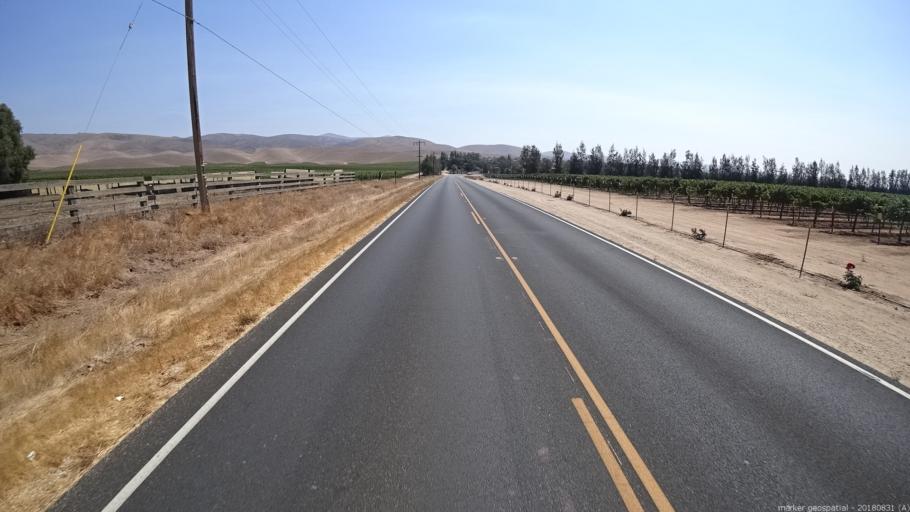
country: US
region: California
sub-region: Monterey County
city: Soledad
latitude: 36.4232
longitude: -121.2896
